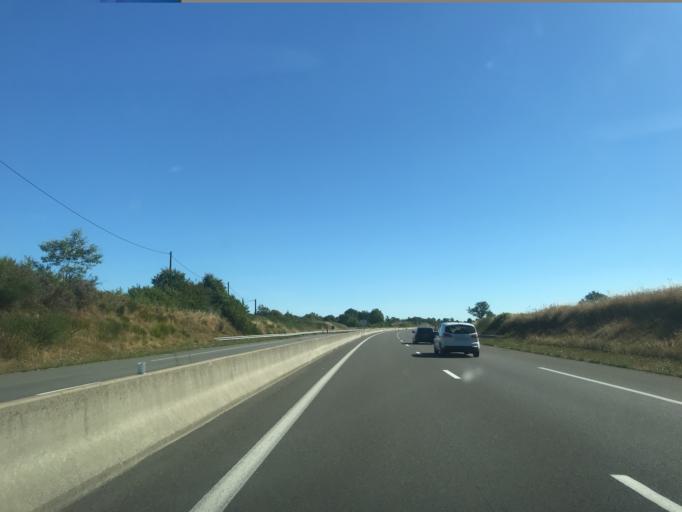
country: FR
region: Limousin
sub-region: Departement de la Creuse
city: Chambon-sur-Voueize
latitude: 46.2875
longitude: 2.4071
